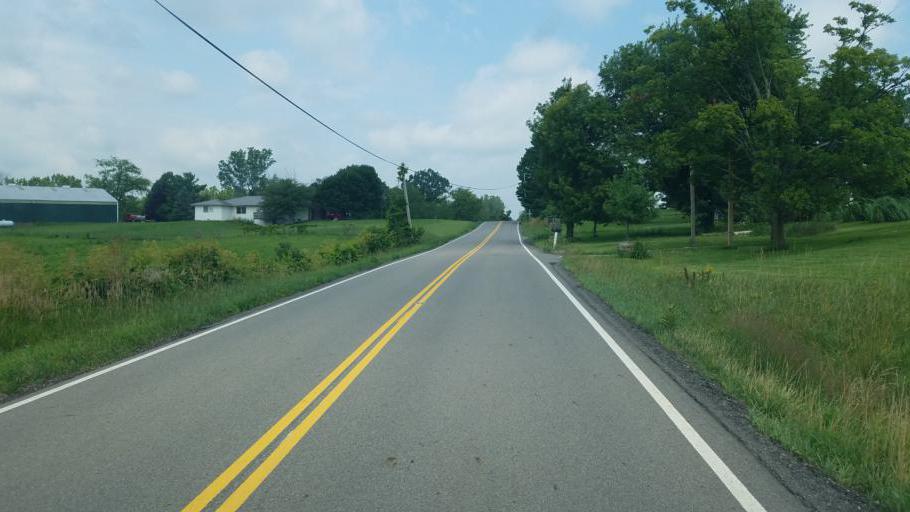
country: US
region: Ohio
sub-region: Knox County
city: Centerburg
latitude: 40.2840
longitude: -82.6244
